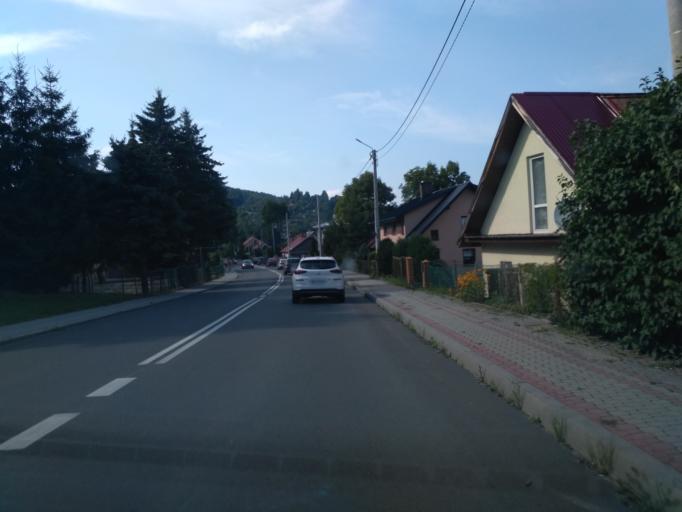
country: PL
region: Subcarpathian Voivodeship
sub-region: Powiat bieszczadzki
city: Ustrzyki Dolne
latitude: 49.4268
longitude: 22.6063
